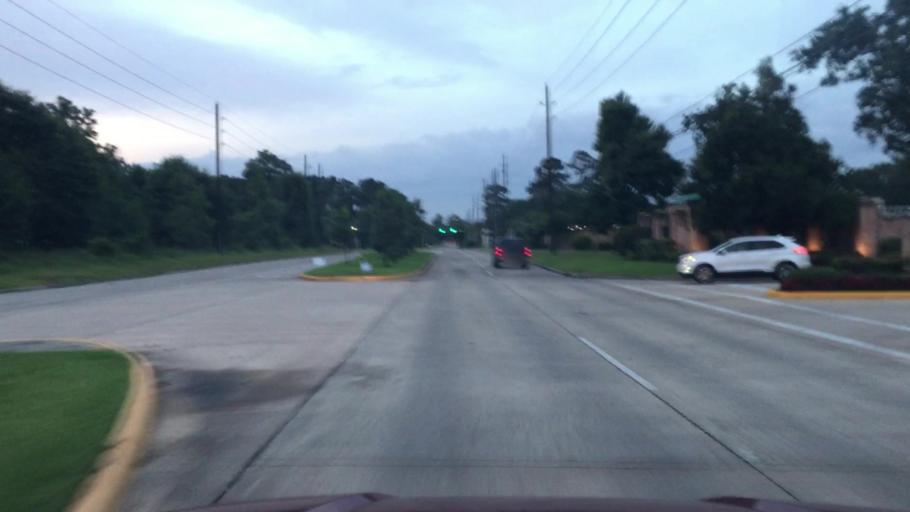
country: US
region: Texas
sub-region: Harris County
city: Tomball
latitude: 30.0324
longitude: -95.5341
